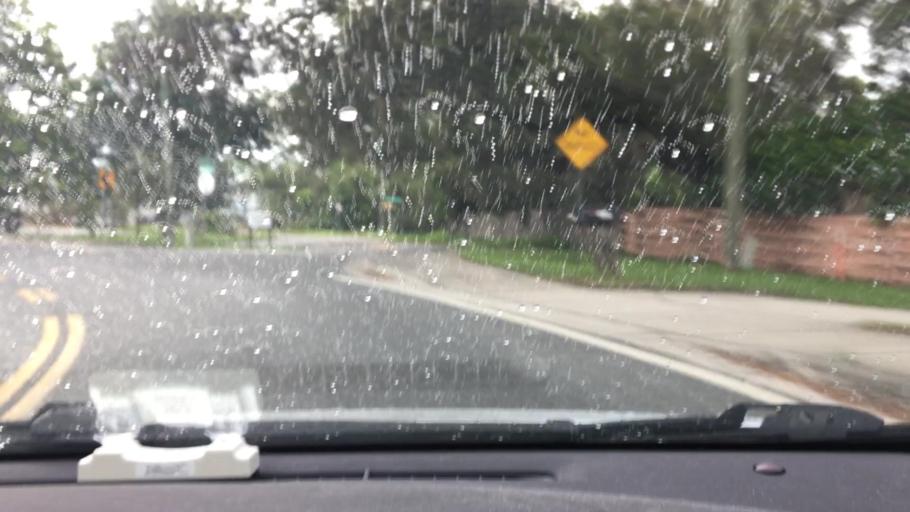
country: US
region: Florida
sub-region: Seminole County
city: Casselberry
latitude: 28.6758
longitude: -81.3460
